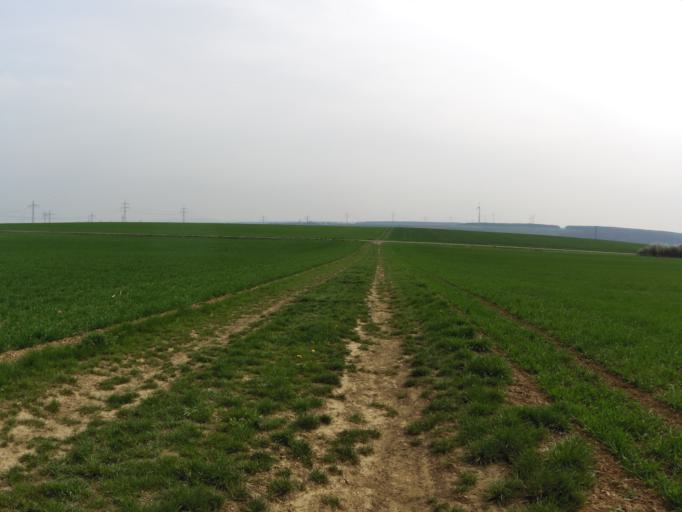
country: DE
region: Bavaria
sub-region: Regierungsbezirk Unterfranken
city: Theilheim
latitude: 49.7712
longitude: 10.0384
